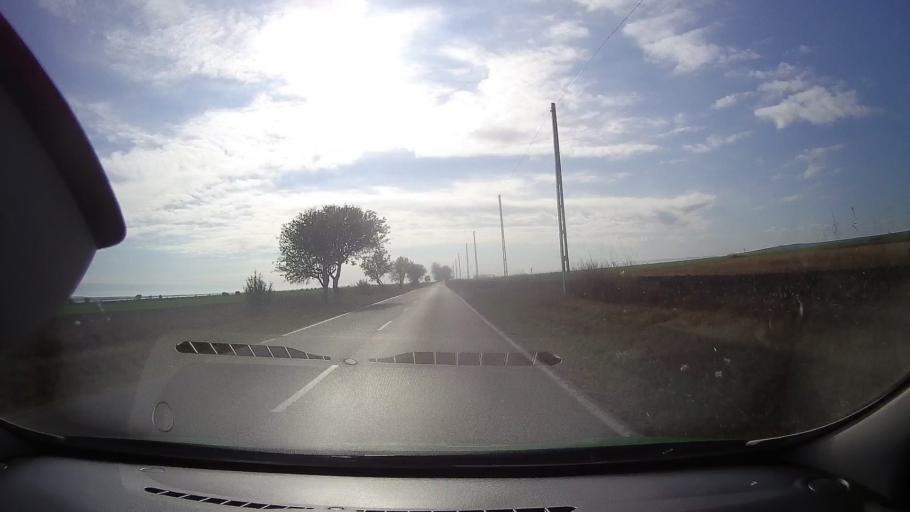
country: RO
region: Tulcea
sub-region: Comuna Valea Nucarilor
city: Agighiol
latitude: 45.0180
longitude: 28.8831
